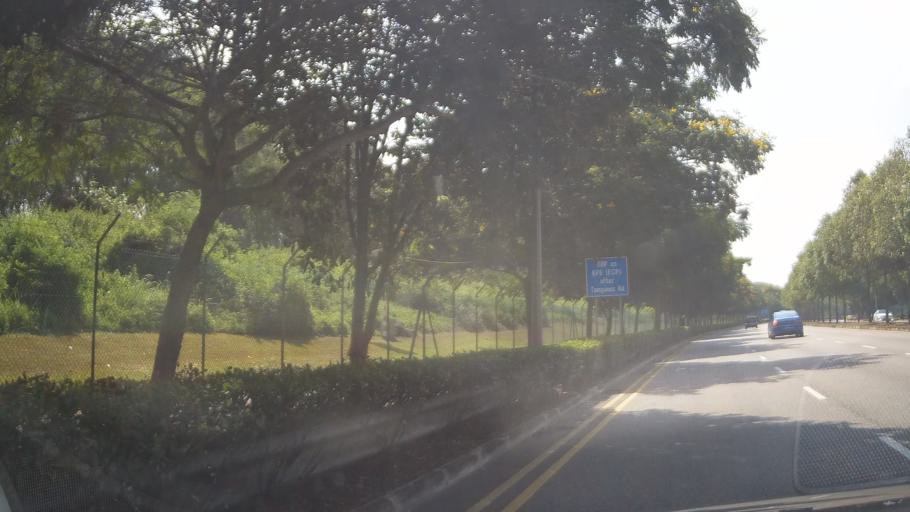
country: MY
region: Johor
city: Kampung Pasir Gudang Baru
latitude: 1.3798
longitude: 103.9064
